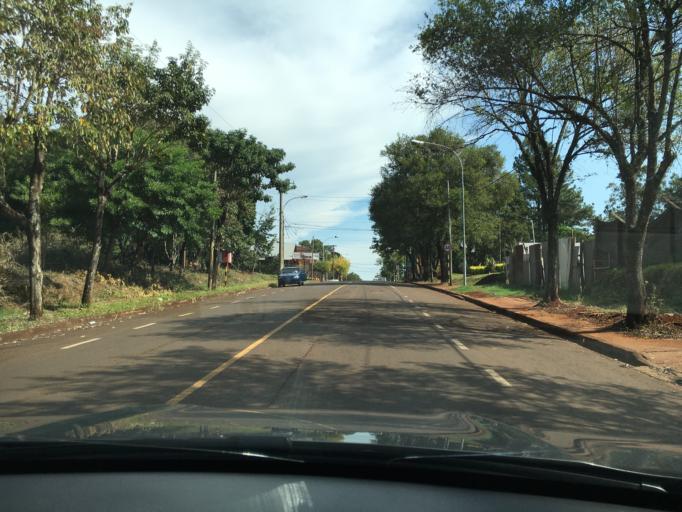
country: AR
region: Misiones
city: Puerto Rico
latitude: -26.8064
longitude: -55.0188
